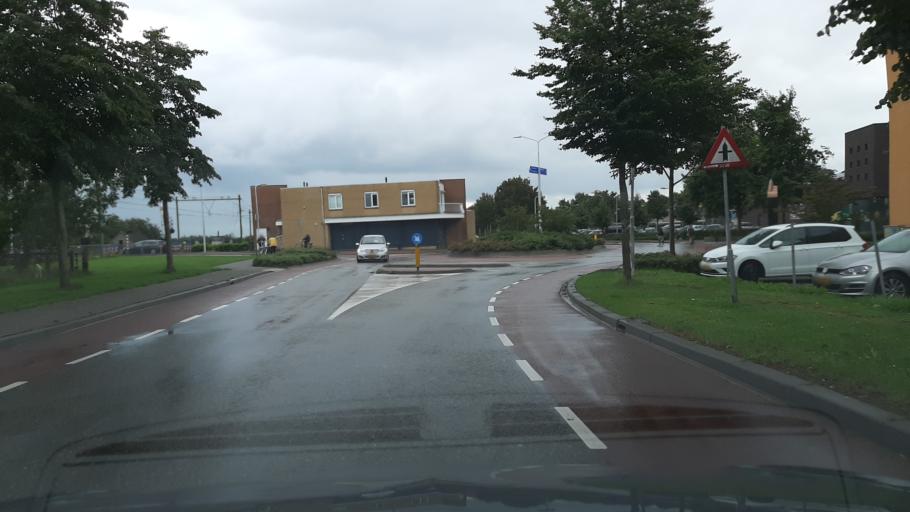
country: NL
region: Friesland
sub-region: Gemeente Weststellingwerf
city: Wolvega
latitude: 52.8782
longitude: 6.0065
